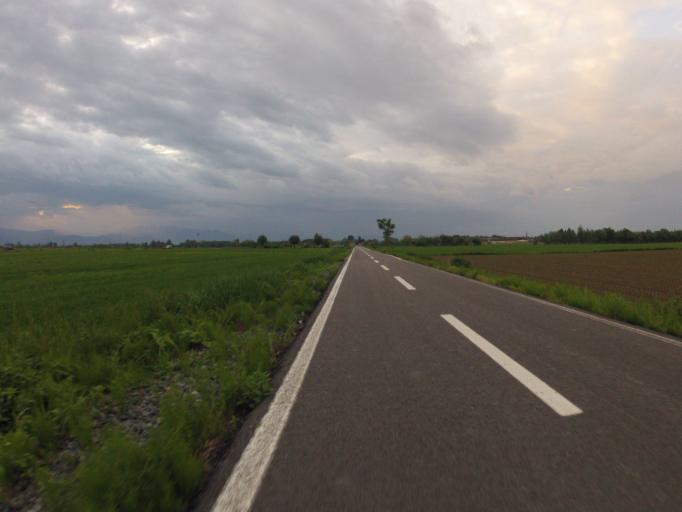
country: IT
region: Piedmont
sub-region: Provincia di Torino
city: Villafranca Piemonte
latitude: 44.8003
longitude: 7.5045
